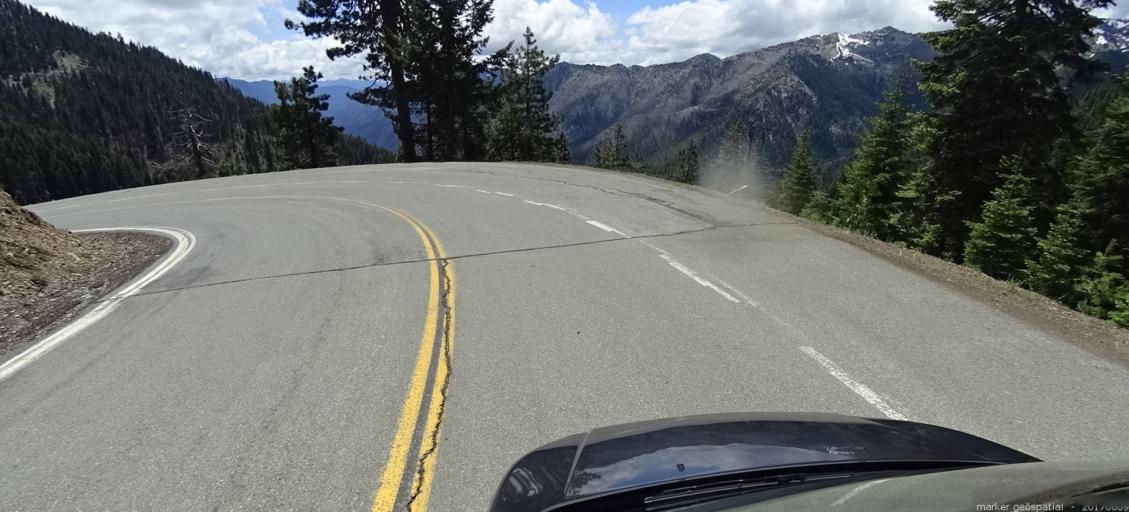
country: US
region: California
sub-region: Siskiyou County
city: Yreka
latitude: 41.3897
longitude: -122.9934
